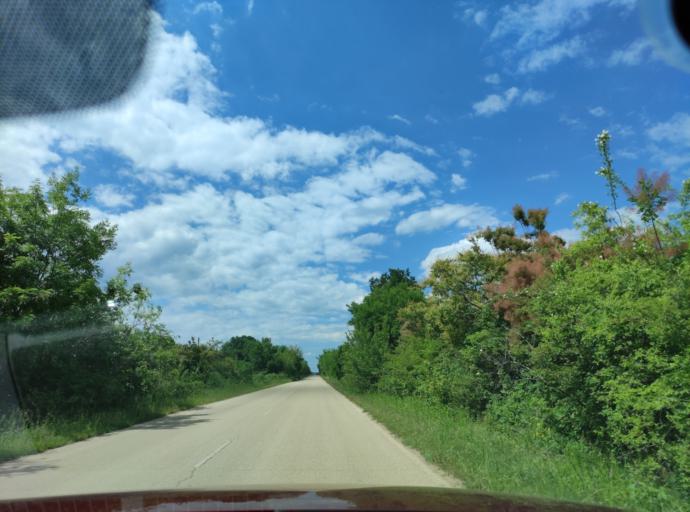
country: BG
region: Montana
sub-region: Obshtina Berkovitsa
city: Berkovitsa
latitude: 43.3631
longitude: 23.0885
